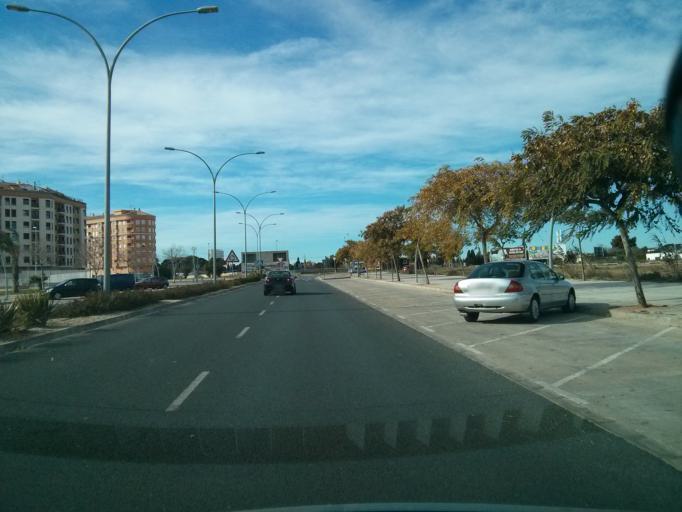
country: ES
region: Valencia
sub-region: Provincia de Castello
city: Castello de la Plana
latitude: 39.9948
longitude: -0.0434
